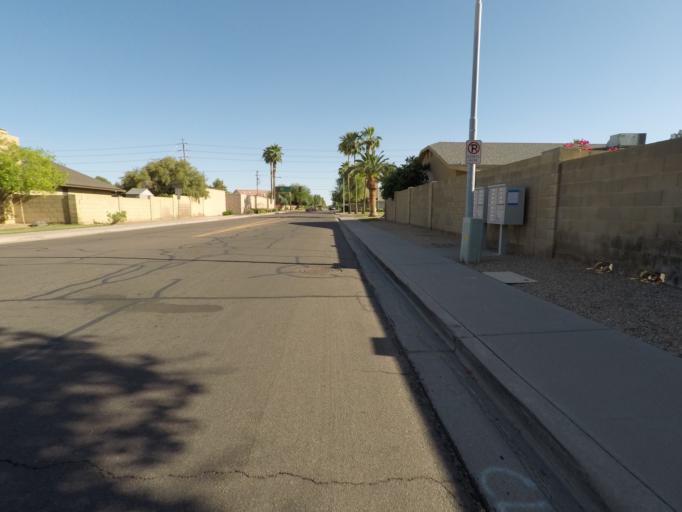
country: US
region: Arizona
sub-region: Maricopa County
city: Guadalupe
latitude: 33.3502
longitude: -111.9199
